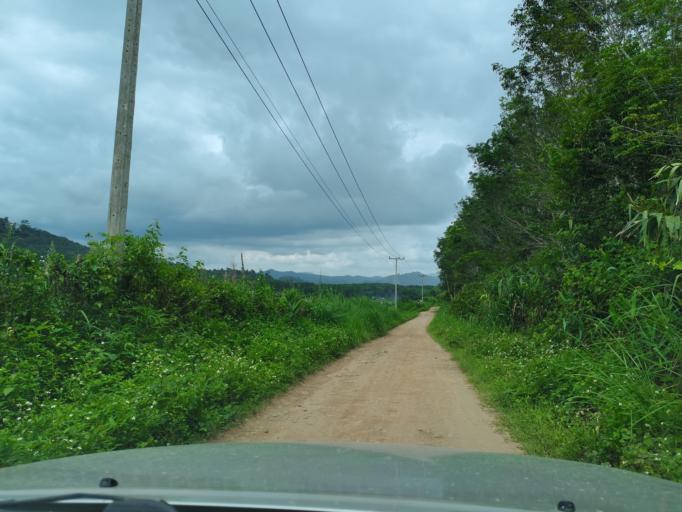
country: LA
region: Loungnamtha
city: Muang Long
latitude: 20.6983
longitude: 101.0370
